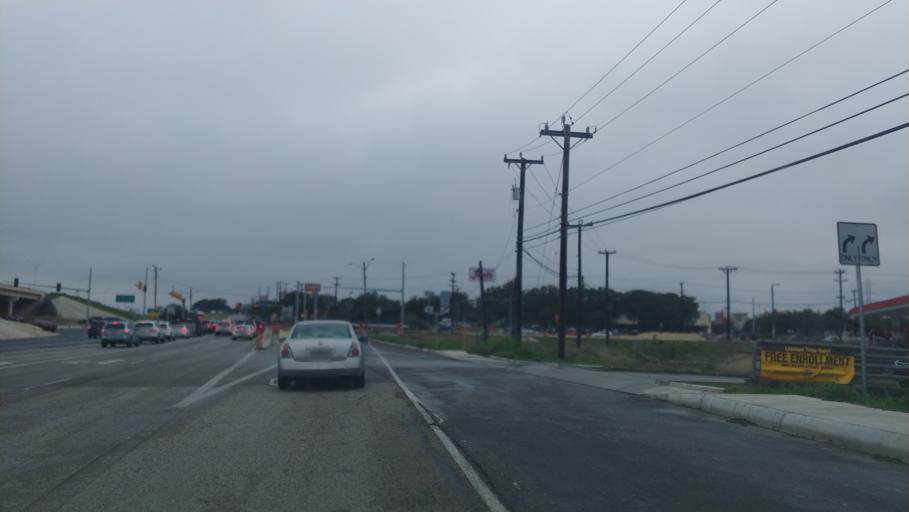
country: US
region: Texas
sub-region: Bexar County
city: Helotes
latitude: 29.5552
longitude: -98.6666
